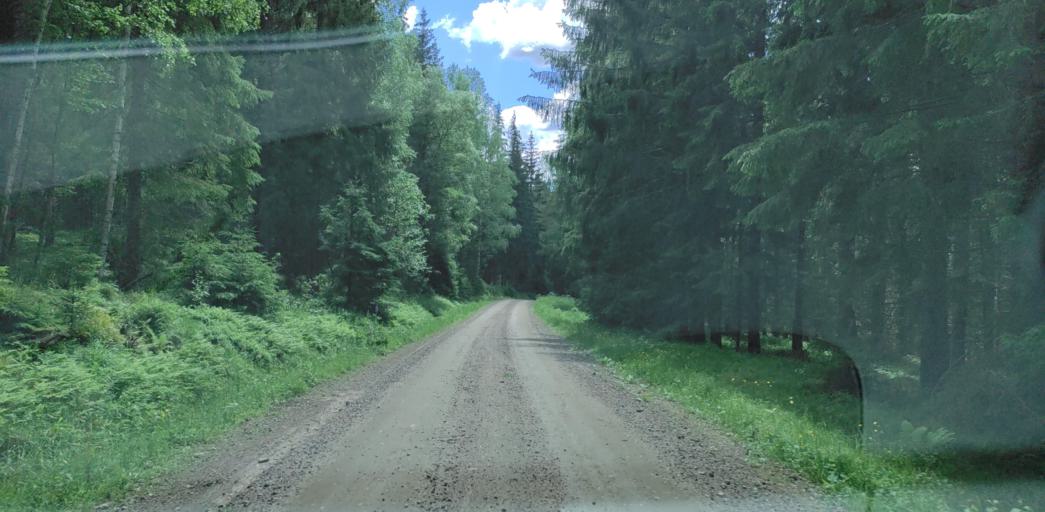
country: SE
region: Vaermland
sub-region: Hagfors Kommun
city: Ekshaerad
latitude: 60.0646
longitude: 13.3071
